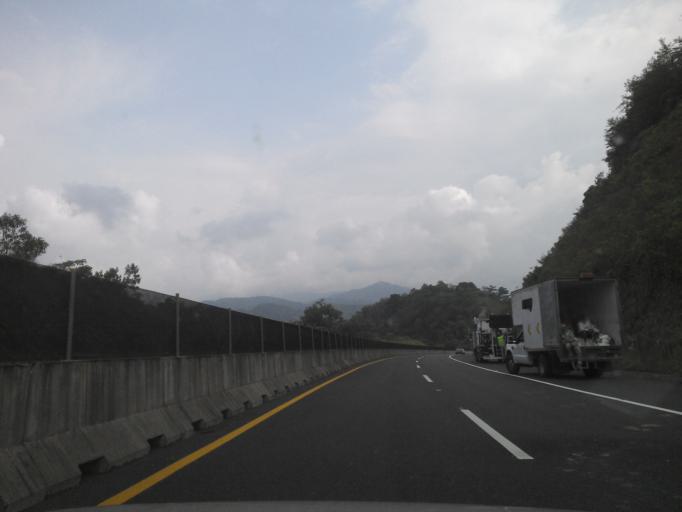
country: MX
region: Puebla
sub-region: Xicotepec
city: San Lorenzo
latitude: 20.3794
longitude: -97.9443
